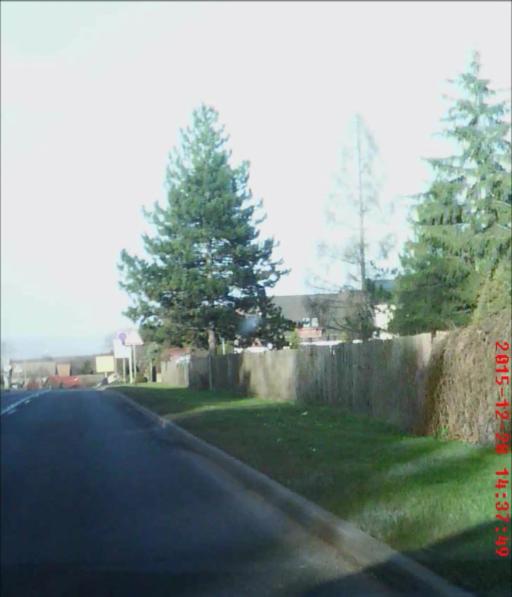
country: DE
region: Thuringia
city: Buttelstedt
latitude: 51.0704
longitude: 11.3410
